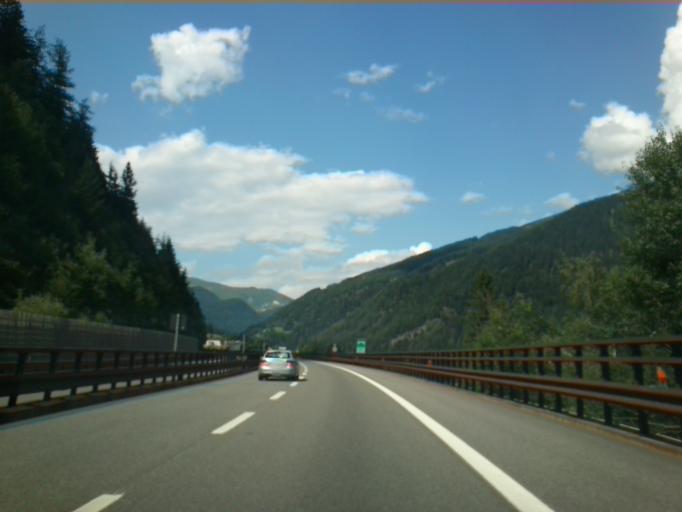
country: IT
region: Trentino-Alto Adige
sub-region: Bolzano
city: Brennero - Brenner
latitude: 46.9188
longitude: 11.4420
